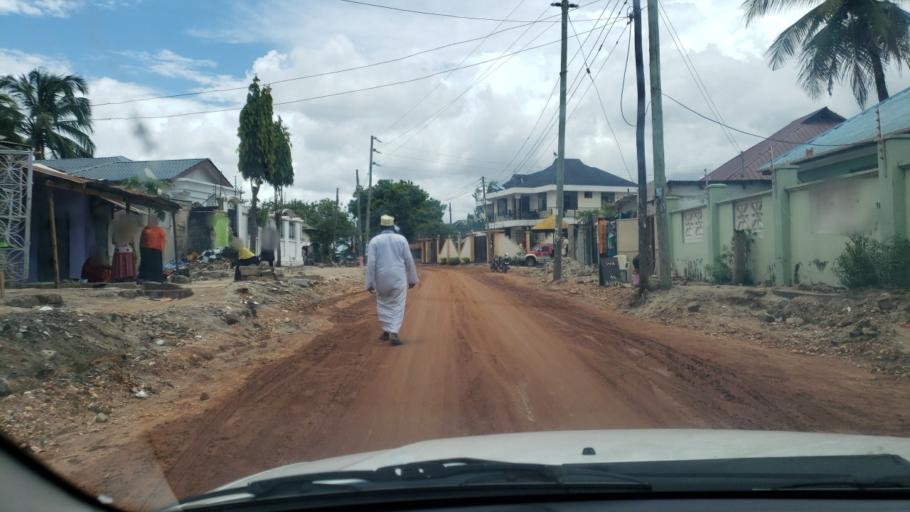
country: TZ
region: Dar es Salaam
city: Magomeni
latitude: -6.8095
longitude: 39.2520
